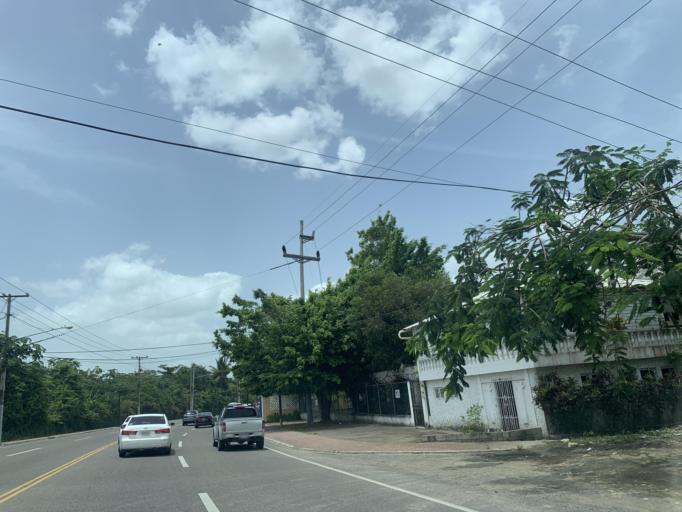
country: DO
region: Puerto Plata
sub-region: Puerto Plata
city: Puerto Plata
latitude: 19.7724
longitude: -70.6551
